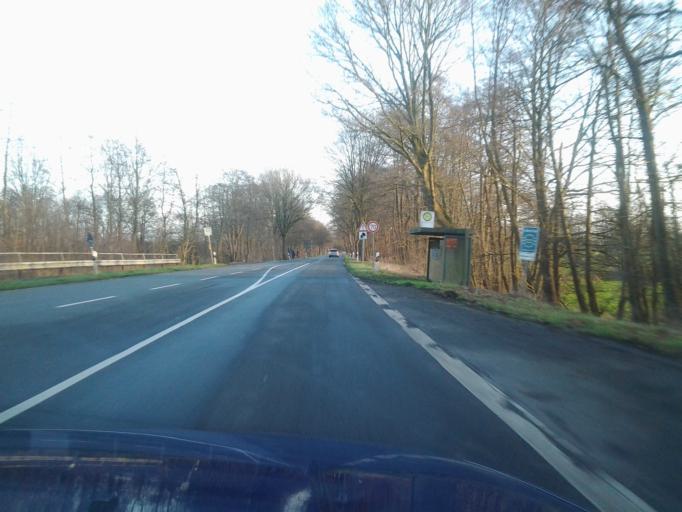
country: DE
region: Lower Saxony
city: Osterholz-Scharmbeck
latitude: 53.1845
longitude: 8.8168
